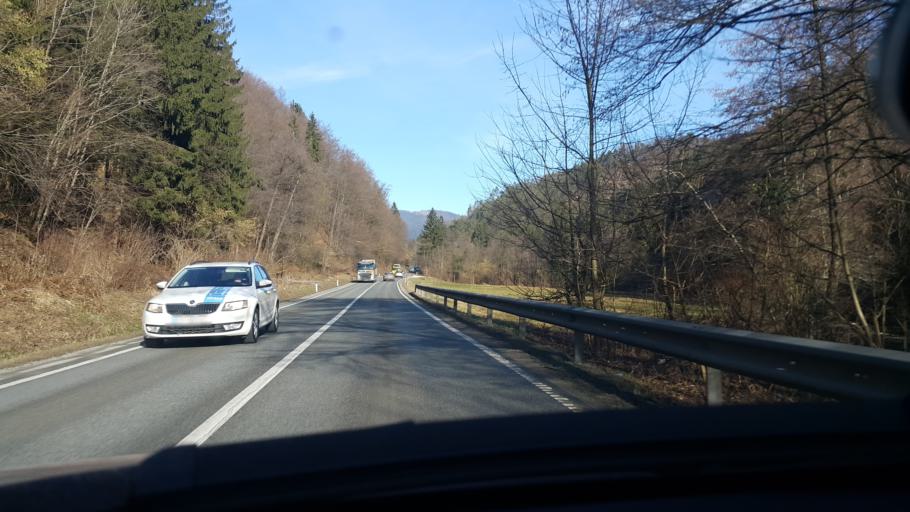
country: SI
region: Zalec
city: Gotovlje
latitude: 46.3013
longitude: 15.1719
